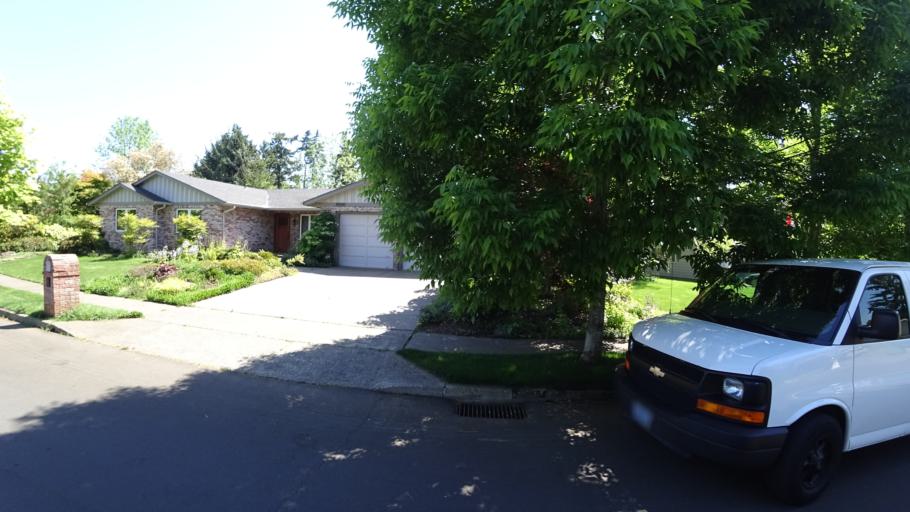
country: US
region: Oregon
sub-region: Washington County
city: Rockcreek
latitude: 45.5489
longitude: -122.8780
